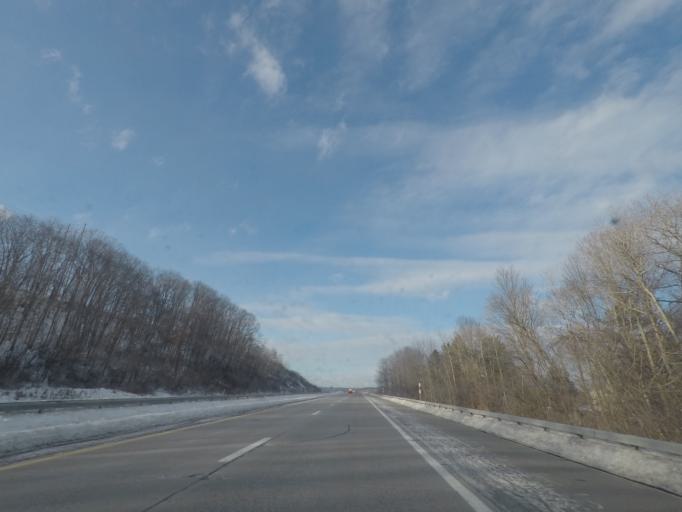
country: US
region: New York
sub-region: Schenectady County
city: Scotia
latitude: 42.8271
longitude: -73.9921
